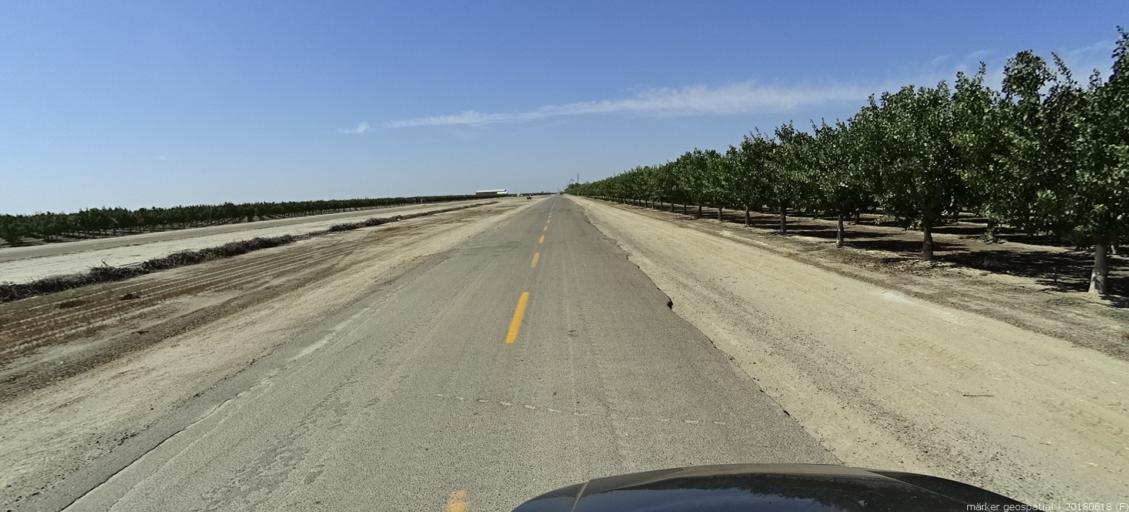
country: US
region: California
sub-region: Fresno County
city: Mendota
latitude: 36.8164
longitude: -120.2591
